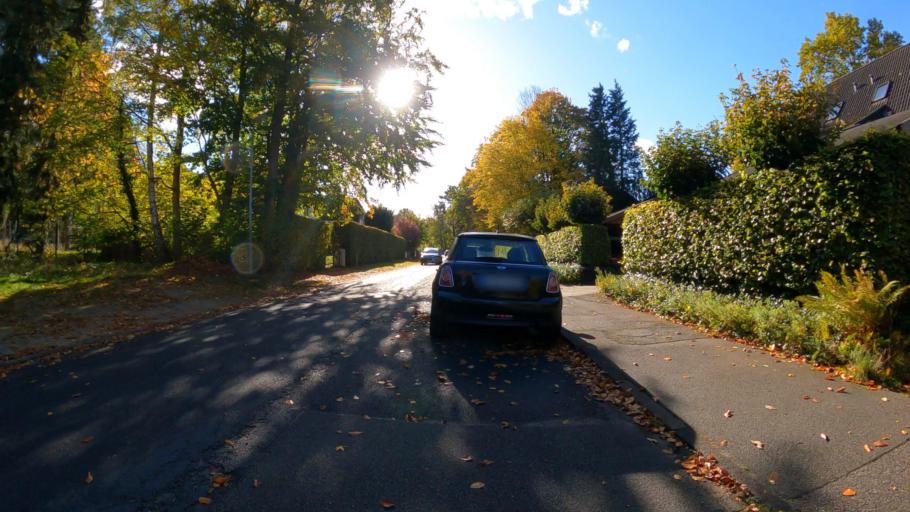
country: DE
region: Schleswig-Holstein
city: Ahrensburg
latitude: 53.6605
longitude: 10.2524
